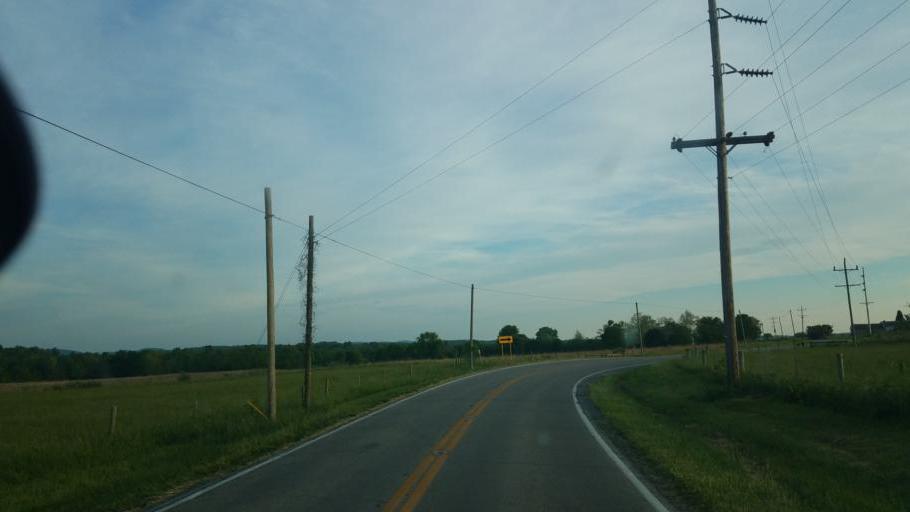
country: US
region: Ohio
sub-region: Highland County
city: Greenfield
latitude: 39.2923
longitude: -83.4101
